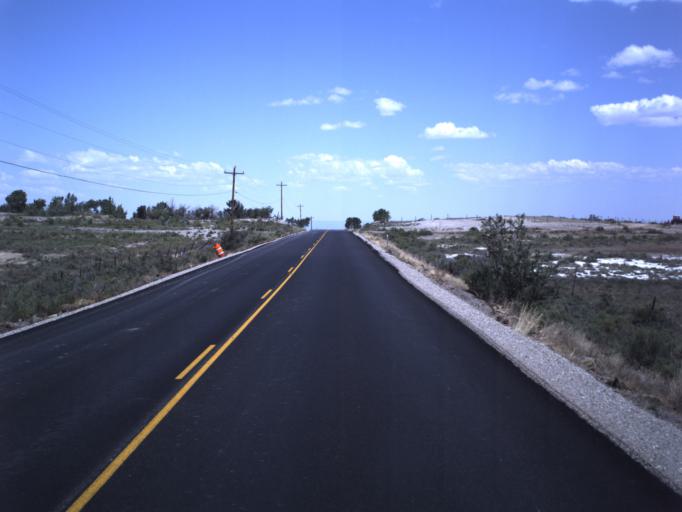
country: US
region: Utah
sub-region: Emery County
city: Castle Dale
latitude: 39.2329
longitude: -111.0129
